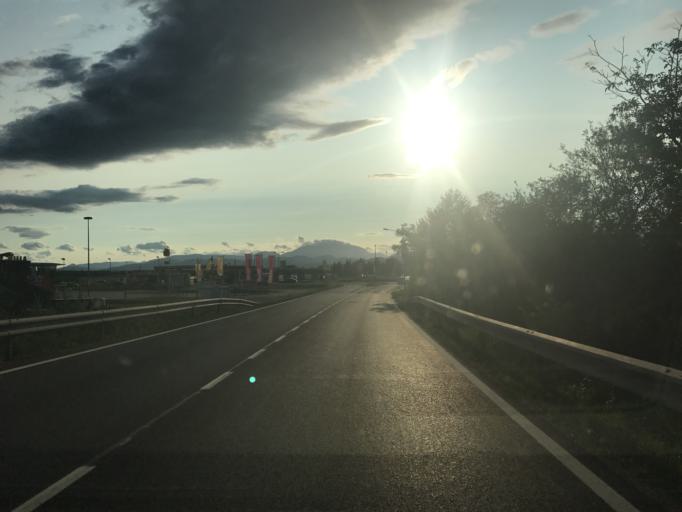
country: AT
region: Lower Austria
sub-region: Wiener Neustadt Stadt
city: Wiener Neustadt
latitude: 47.8058
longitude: 16.2138
